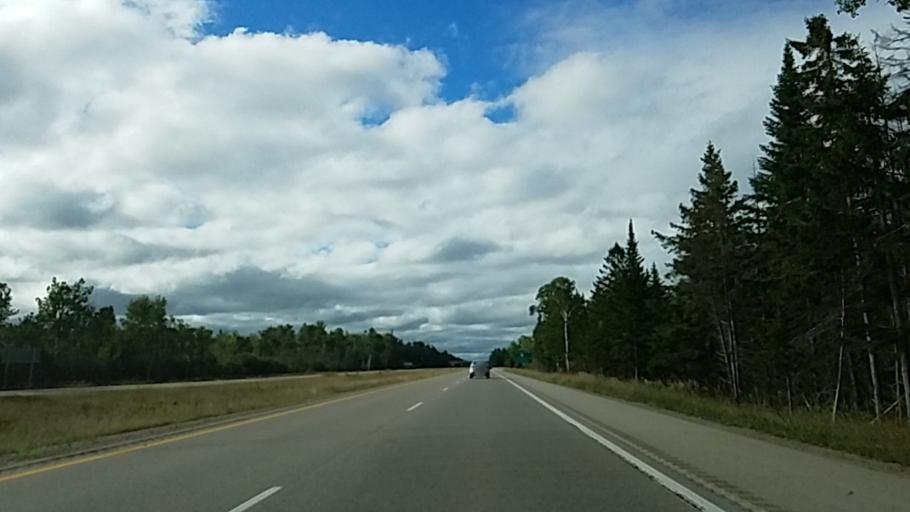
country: US
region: Michigan
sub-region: Mackinac County
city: Saint Ignace
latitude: 45.7410
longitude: -84.7289
